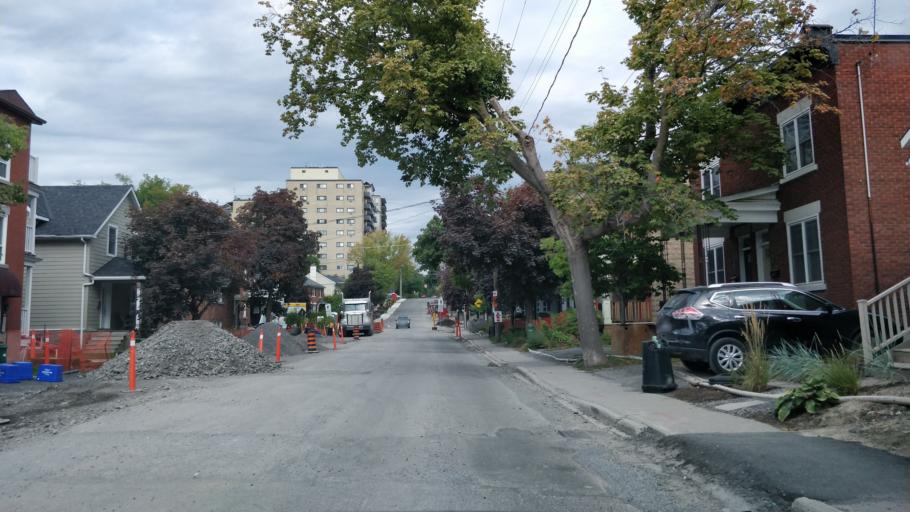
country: CA
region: Ontario
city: Ottawa
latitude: 45.4413
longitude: -75.6767
